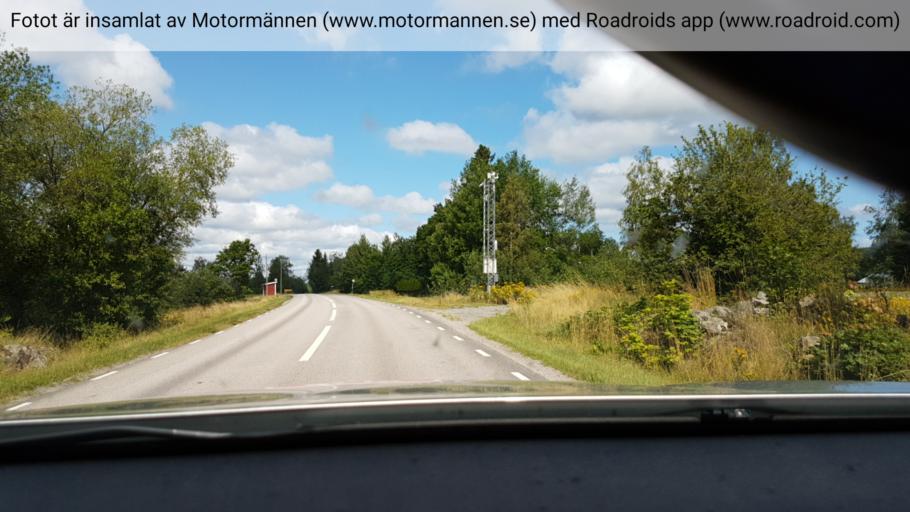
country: SE
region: Stockholm
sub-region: Norrtalje Kommun
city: Arno
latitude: 59.9895
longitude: 18.8098
